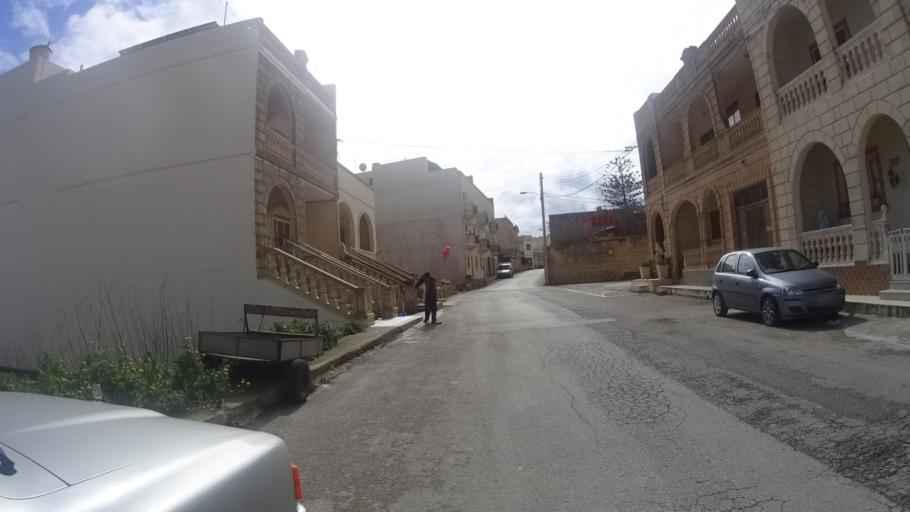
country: MT
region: In-Nadur
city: Nadur
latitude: 36.0433
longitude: 14.2984
